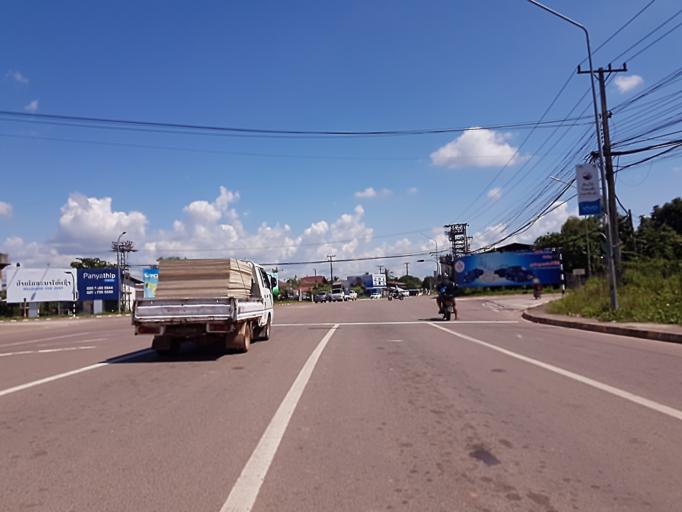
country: TH
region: Nong Khai
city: Tha Bo
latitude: 17.8943
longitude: 102.6437
